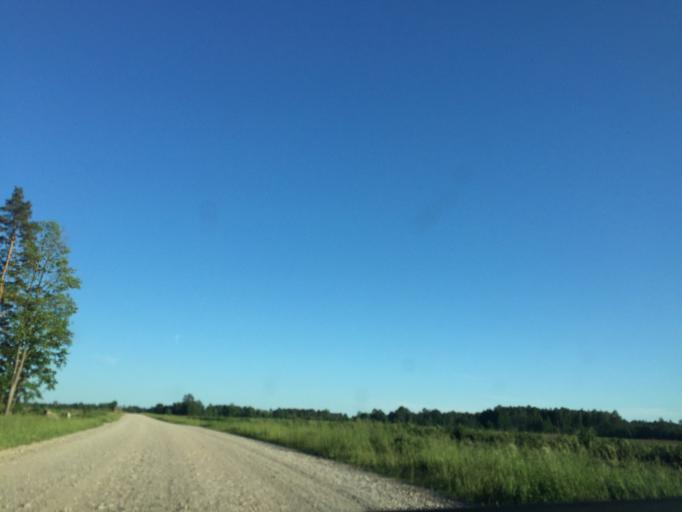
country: LV
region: Broceni
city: Broceni
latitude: 56.8480
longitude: 22.5643
